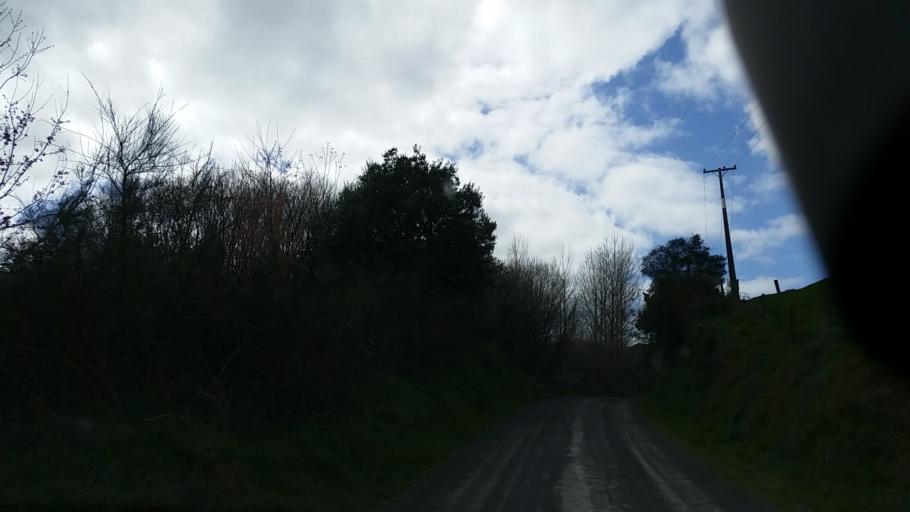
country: NZ
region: Bay of Plenty
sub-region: Rotorua District
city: Rotorua
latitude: -38.2986
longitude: 176.2765
